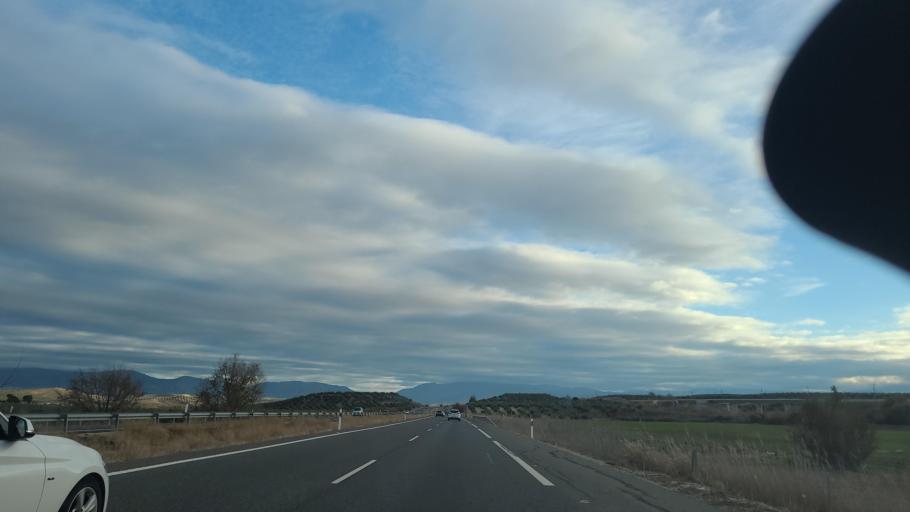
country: ES
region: Andalusia
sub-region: Provincia de Jaen
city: Mengibar
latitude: 37.8800
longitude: -3.7708
